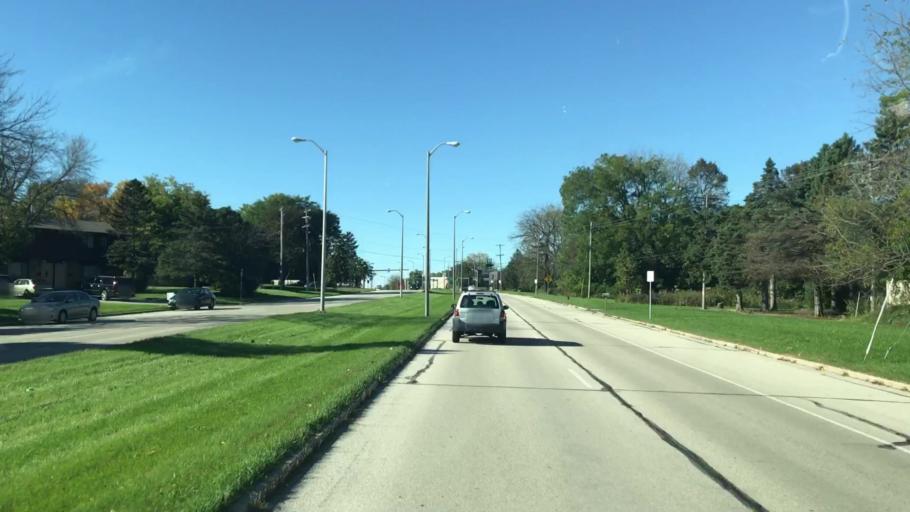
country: US
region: Wisconsin
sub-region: Milwaukee County
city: Hales Corners
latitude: 42.9465
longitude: -88.0334
